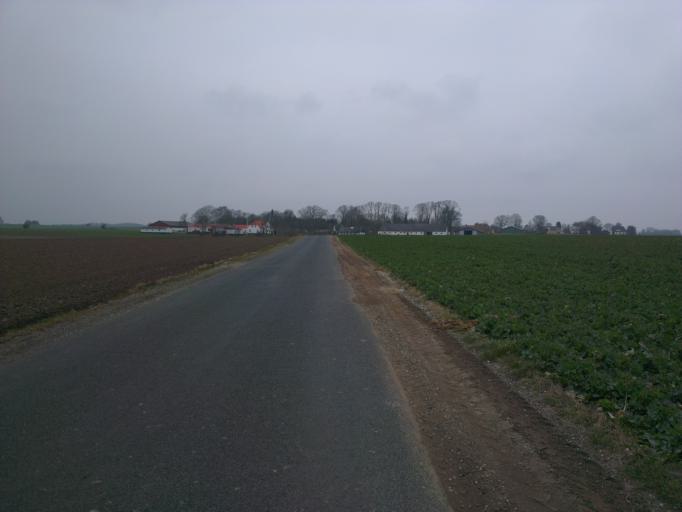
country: DK
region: Capital Region
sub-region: Egedal Kommune
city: Olstykke
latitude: 55.8311
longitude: 12.1196
